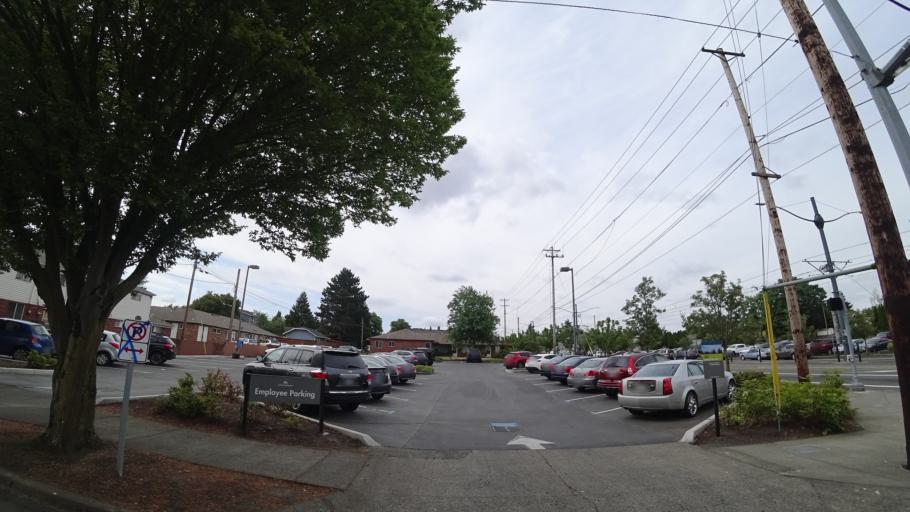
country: US
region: Oregon
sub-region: Multnomah County
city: Portland
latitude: 45.5752
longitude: -122.6819
